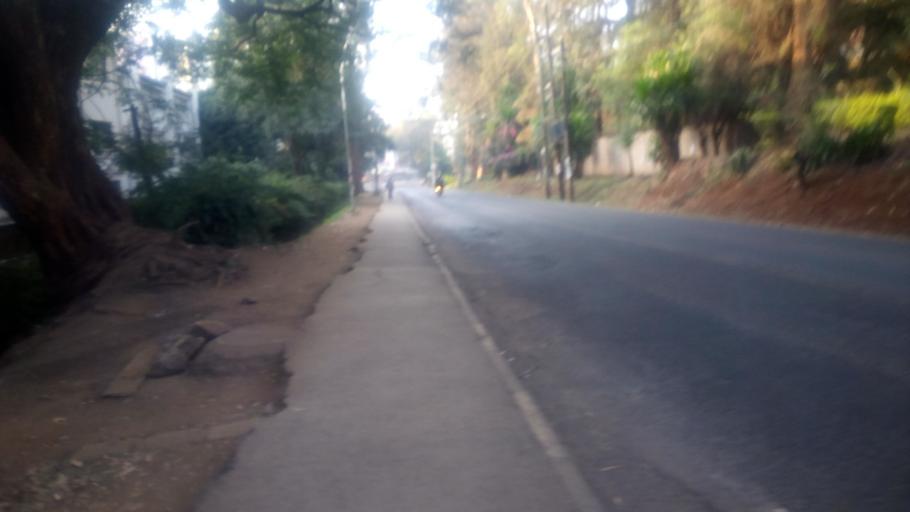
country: KE
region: Nairobi Area
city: Nairobi
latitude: -1.2807
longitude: 36.8129
